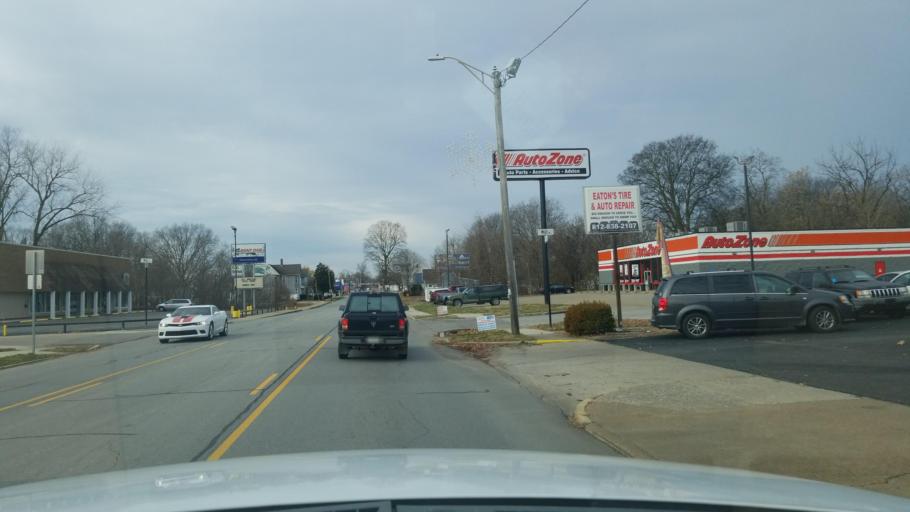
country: US
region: Indiana
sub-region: Posey County
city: Mount Vernon
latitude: 37.9317
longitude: -87.8977
